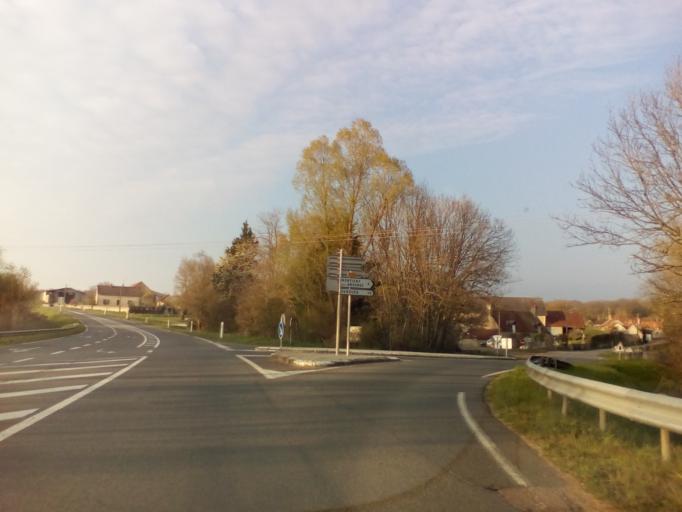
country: FR
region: Bourgogne
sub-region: Departement de la Nievre
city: Urzy
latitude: 47.0236
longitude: 3.2120
